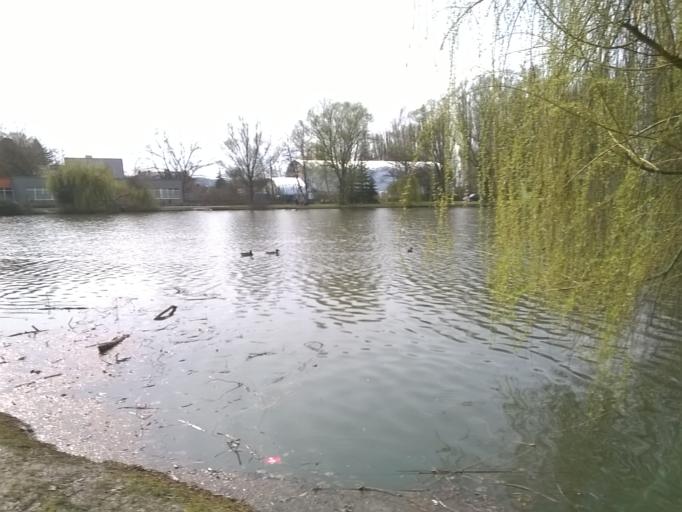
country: SK
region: Nitriansky
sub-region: Okres Nitra
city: Nitra
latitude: 48.3147
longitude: 18.0796
